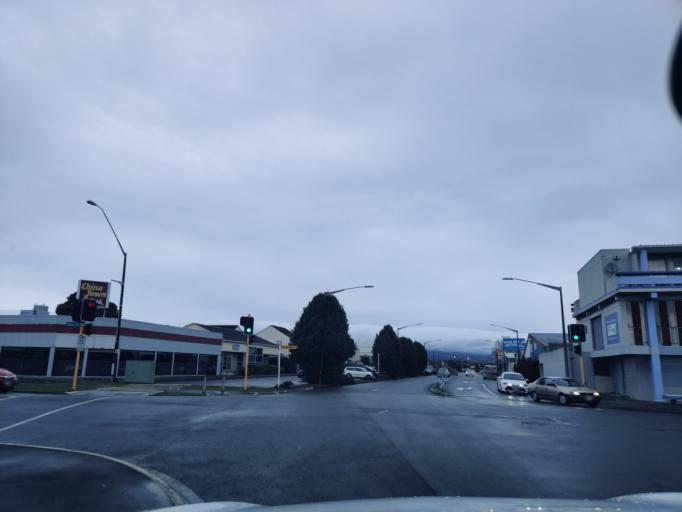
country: NZ
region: Manawatu-Wanganui
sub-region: Palmerston North City
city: Palmerston North
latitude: -40.3565
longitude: 175.6051
